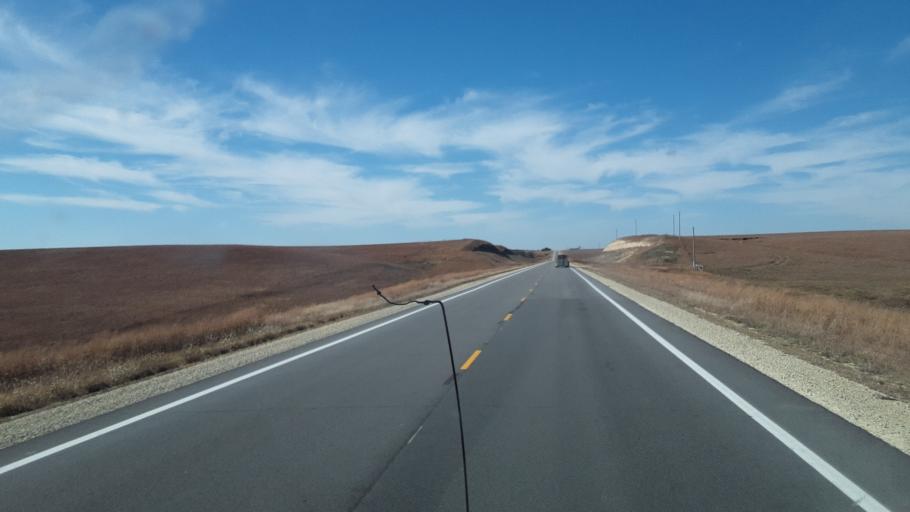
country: US
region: Kansas
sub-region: Chase County
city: Cottonwood Falls
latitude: 38.3628
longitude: -96.7746
